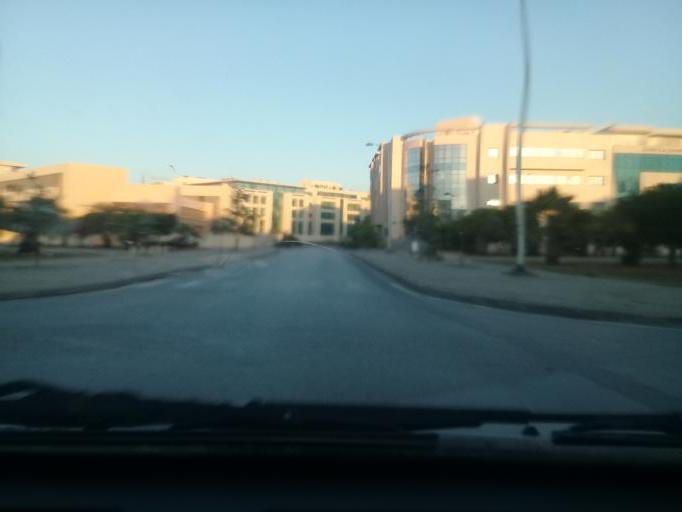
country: TN
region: Tunis
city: La Goulette
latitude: 36.8448
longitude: 10.2771
